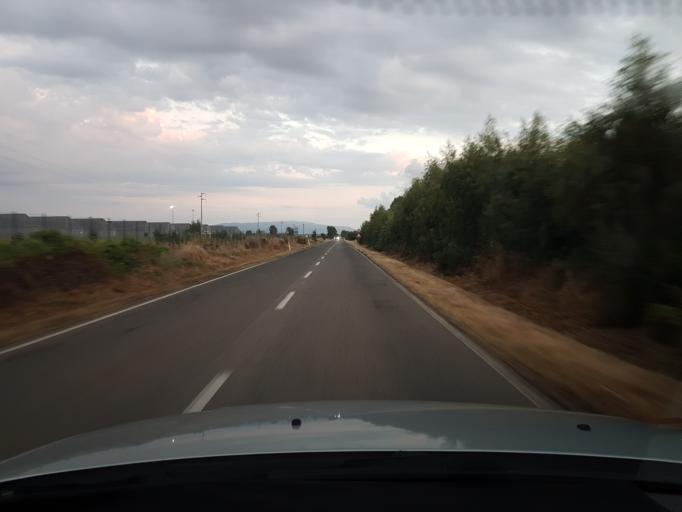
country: IT
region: Sardinia
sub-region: Provincia di Oristano
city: Milis
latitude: 40.0315
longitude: 8.6392
